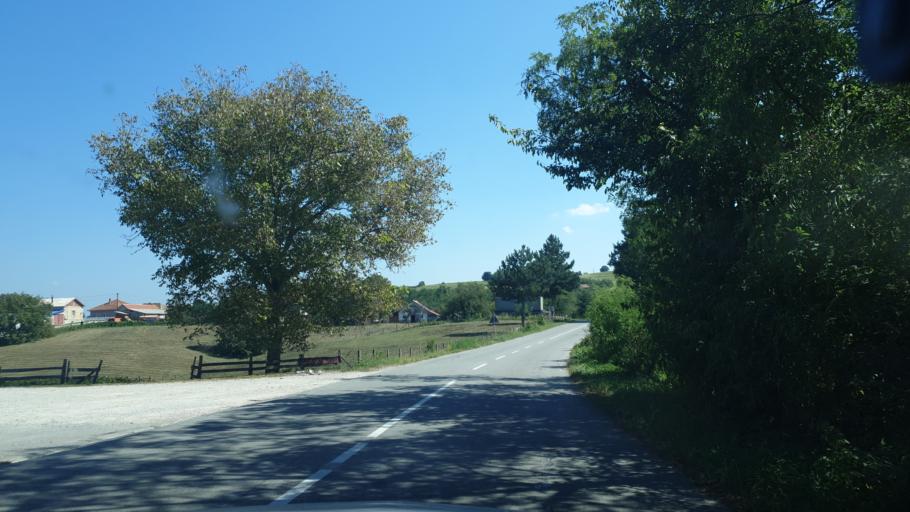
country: RS
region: Central Serbia
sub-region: Kolubarski Okrug
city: Mionica
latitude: 44.1893
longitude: 20.0318
